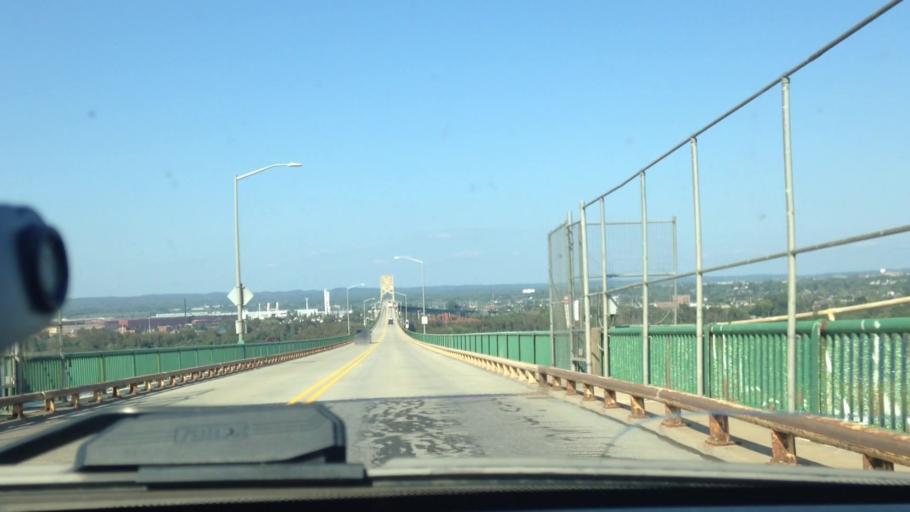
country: US
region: Michigan
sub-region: Chippewa County
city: Sault Ste. Marie
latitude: 46.5045
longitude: -84.3623
